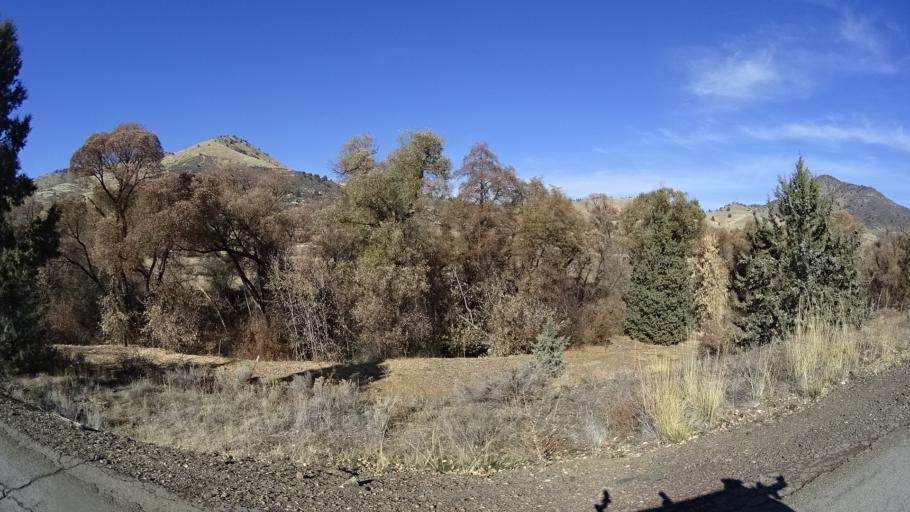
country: US
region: California
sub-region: Siskiyou County
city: Yreka
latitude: 41.7723
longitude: -122.6010
